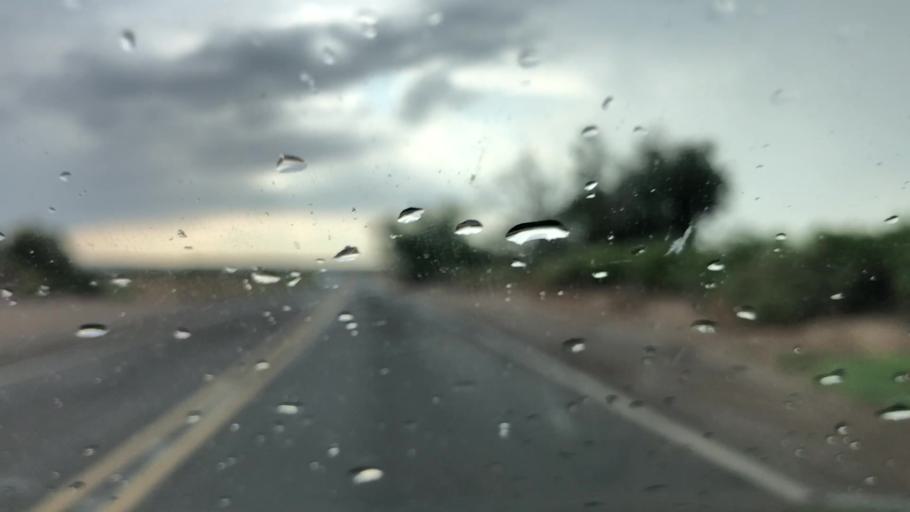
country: US
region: New Mexico
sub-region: Dona Ana County
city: Vado
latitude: 32.0686
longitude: -106.6803
